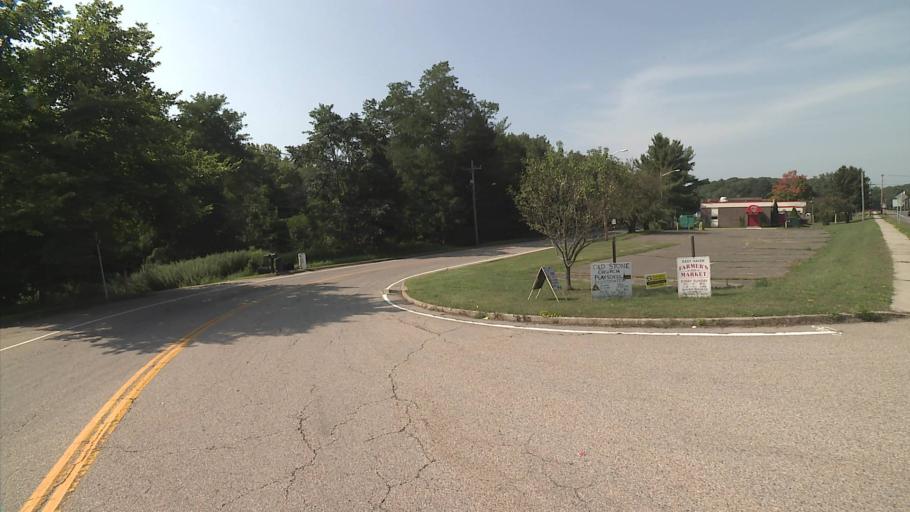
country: US
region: Connecticut
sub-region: New Haven County
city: Branford
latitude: 41.3241
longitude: -72.8382
